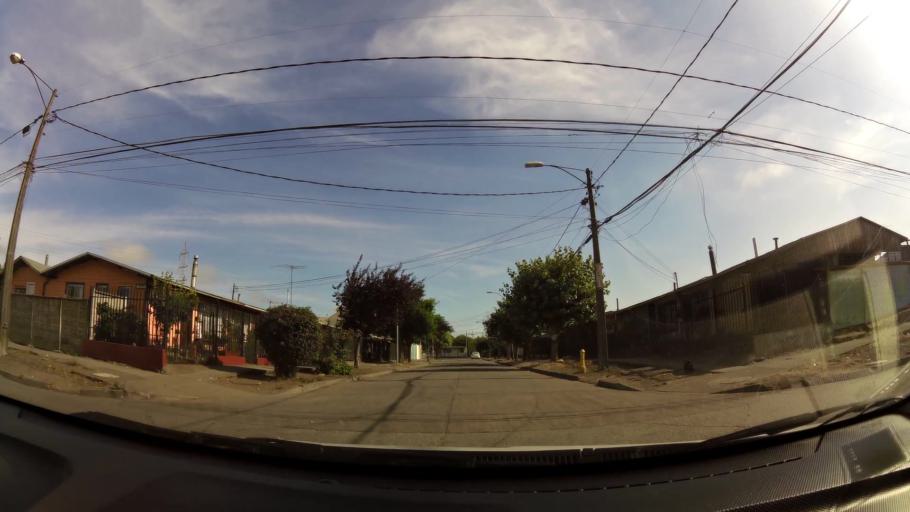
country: CL
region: Biobio
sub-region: Provincia de Concepcion
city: Talcahuano
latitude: -36.7818
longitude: -73.1153
